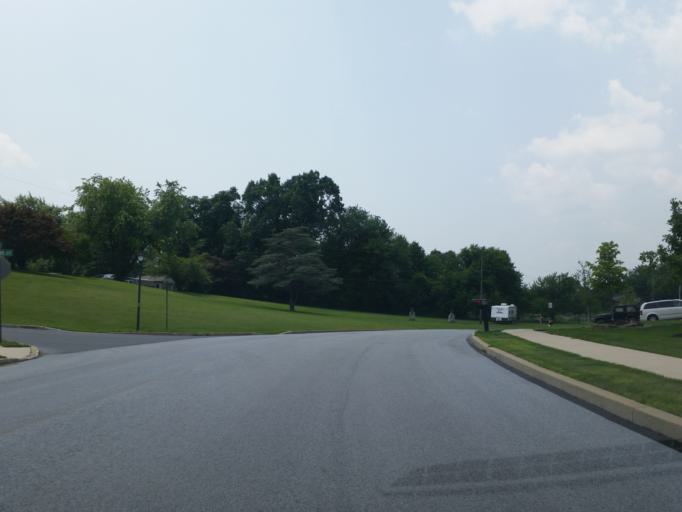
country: US
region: Pennsylvania
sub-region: Lebanon County
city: Campbelltown
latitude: 40.2721
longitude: -76.5879
